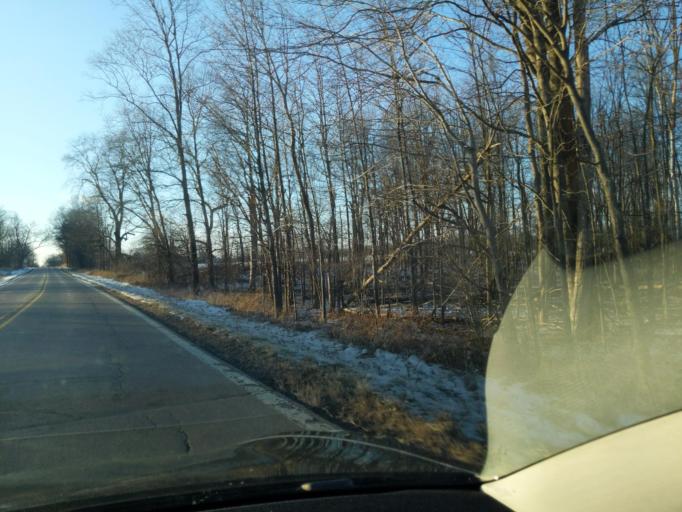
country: US
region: Michigan
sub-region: Ingham County
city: Stockbridge
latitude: 42.4538
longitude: -84.1407
